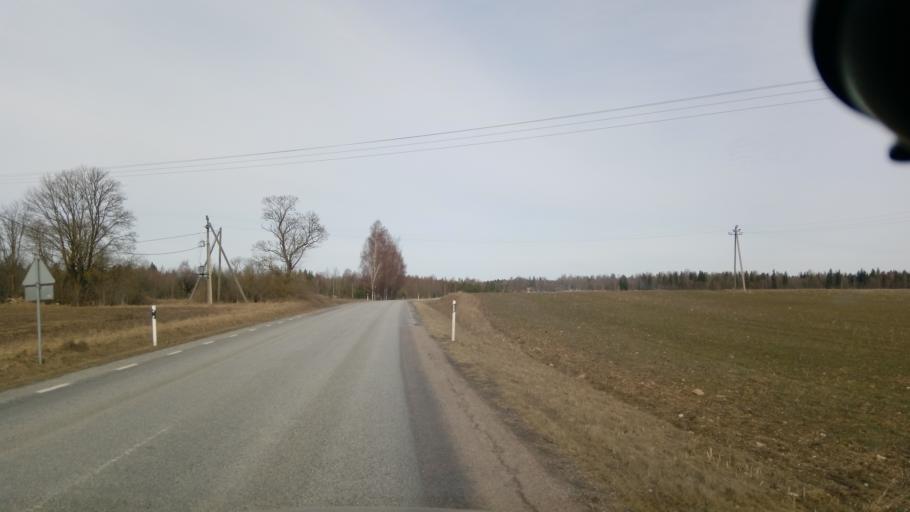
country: EE
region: Raplamaa
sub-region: Rapla vald
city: Rapla
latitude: 59.0331
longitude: 24.8356
